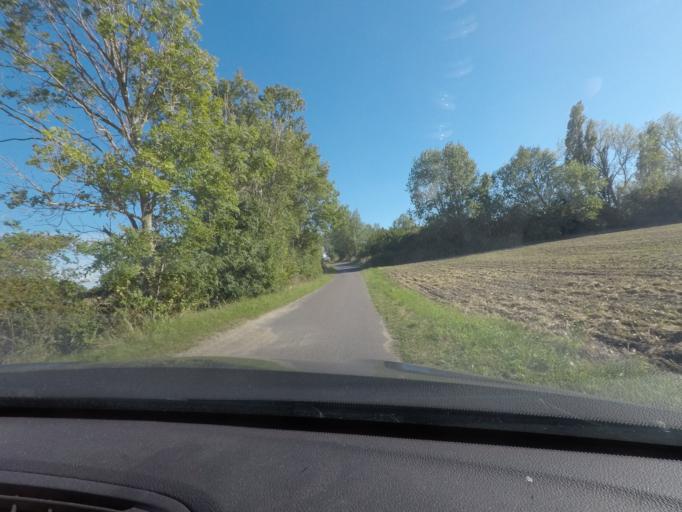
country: DK
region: Zealand
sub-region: Lolland Kommune
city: Maribo
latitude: 54.9775
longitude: 11.5232
